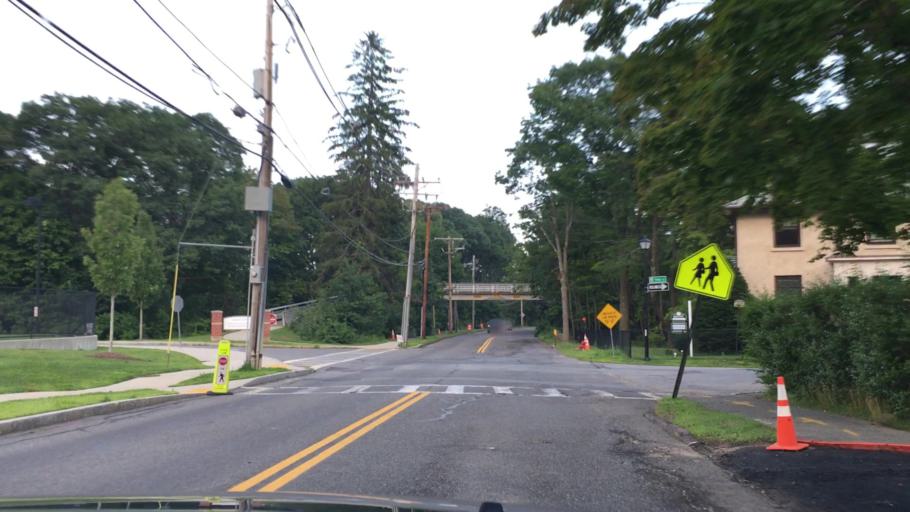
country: US
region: Massachusetts
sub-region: Essex County
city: Essex
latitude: 42.5806
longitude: -70.7658
